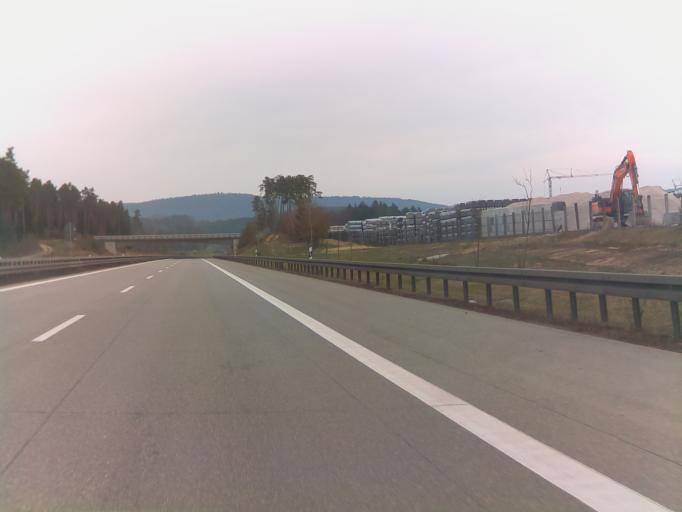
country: DE
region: Bavaria
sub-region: Upper Palatinate
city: Ebermannsdorf
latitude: 49.4135
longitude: 11.9924
